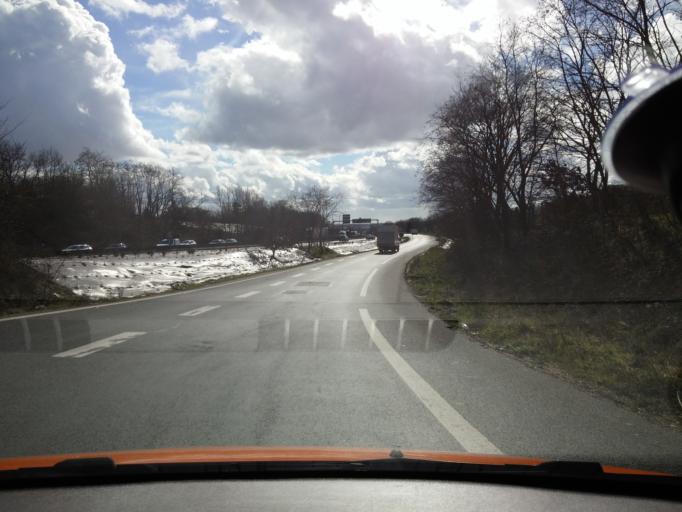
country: FR
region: Ile-de-France
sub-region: Departement de l'Essonne
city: Chilly-Mazarin
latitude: 48.7089
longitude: 2.3062
